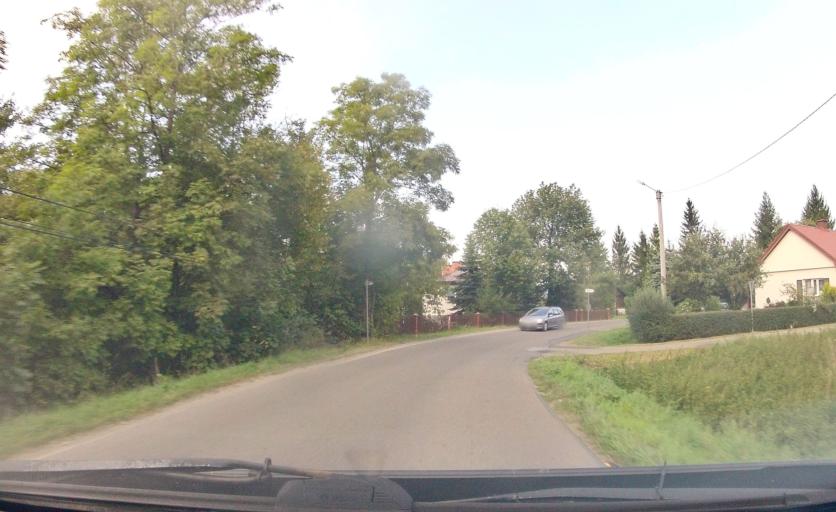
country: PL
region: Subcarpathian Voivodeship
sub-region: Powiat krosnienski
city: Dukla
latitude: 49.5528
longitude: 21.6214
